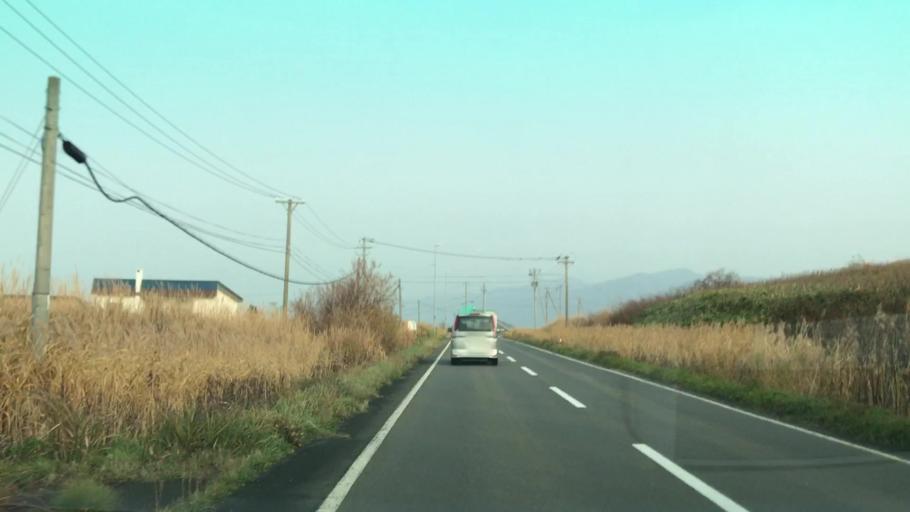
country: JP
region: Hokkaido
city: Ishikari
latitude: 43.3697
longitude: 141.4268
